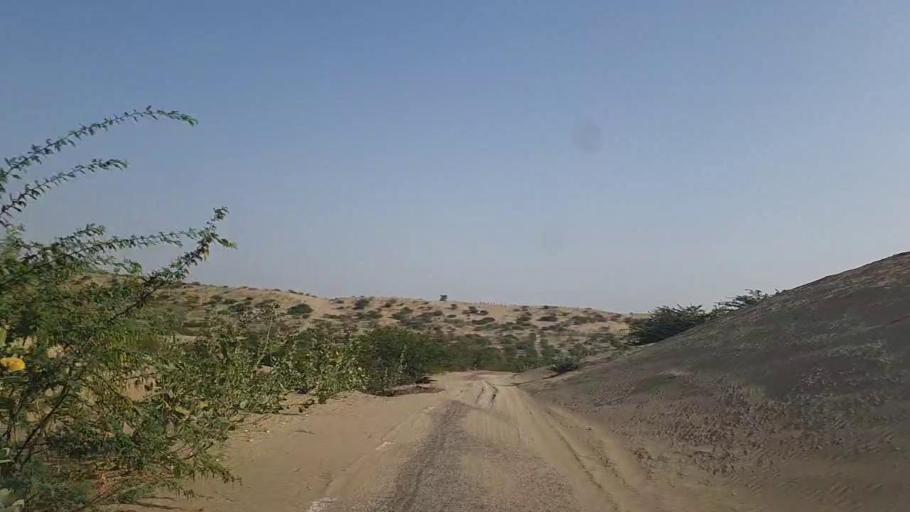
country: PK
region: Sindh
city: Naukot
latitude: 24.6224
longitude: 69.3702
